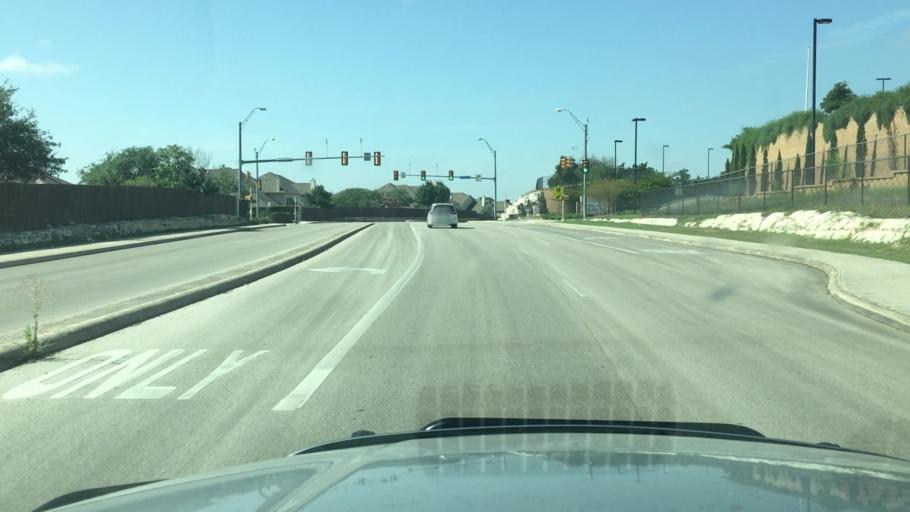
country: US
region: Texas
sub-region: Bexar County
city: Timberwood Park
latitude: 29.6731
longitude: -98.4548
